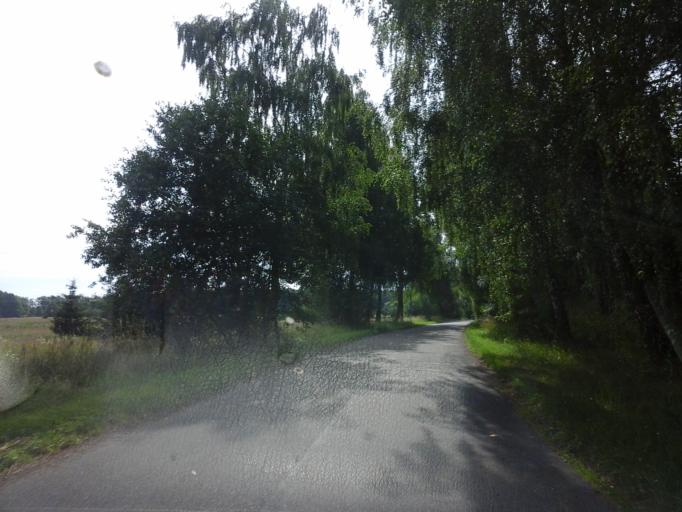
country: PL
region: West Pomeranian Voivodeship
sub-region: Powiat choszczenski
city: Bierzwnik
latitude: 53.0484
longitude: 15.6186
